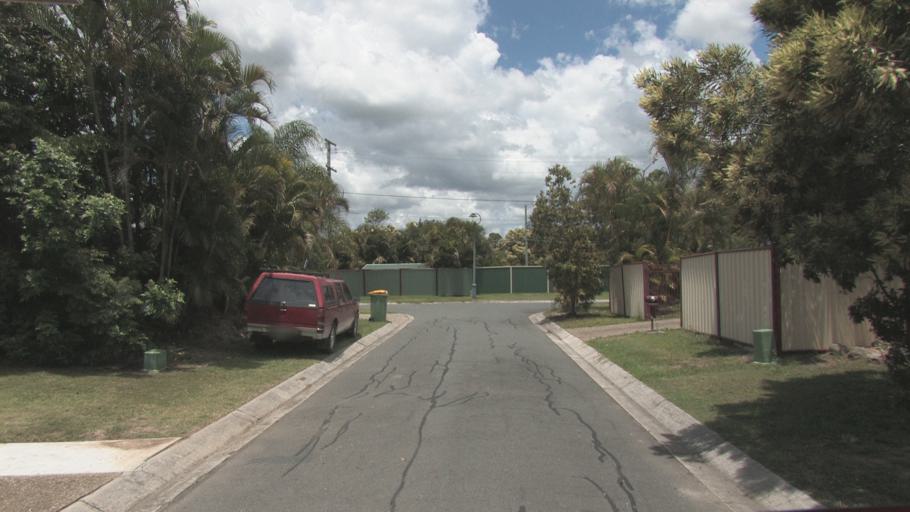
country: AU
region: Queensland
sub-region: Logan
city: Waterford West
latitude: -27.6906
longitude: 153.1299
